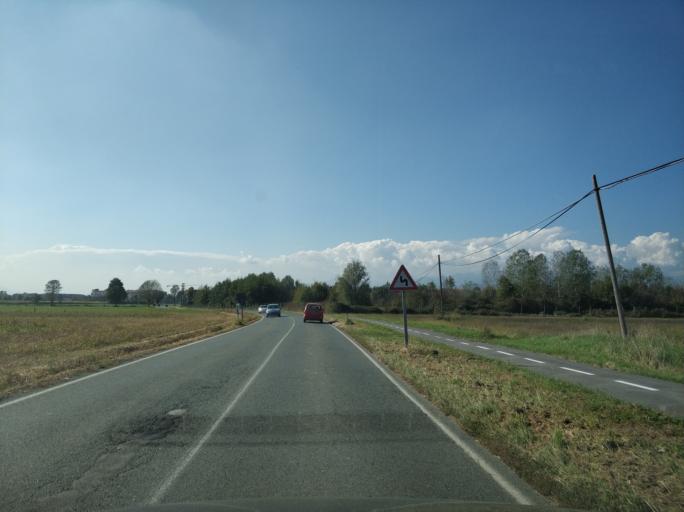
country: IT
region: Piedmont
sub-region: Provincia di Torino
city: Borgaro Torinese
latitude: 45.1519
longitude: 7.6728
